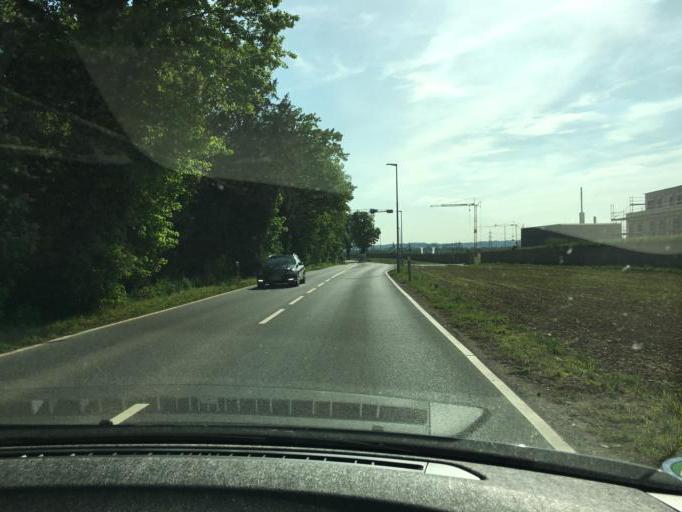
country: DE
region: North Rhine-Westphalia
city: Wesseling
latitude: 50.8023
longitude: 6.9876
